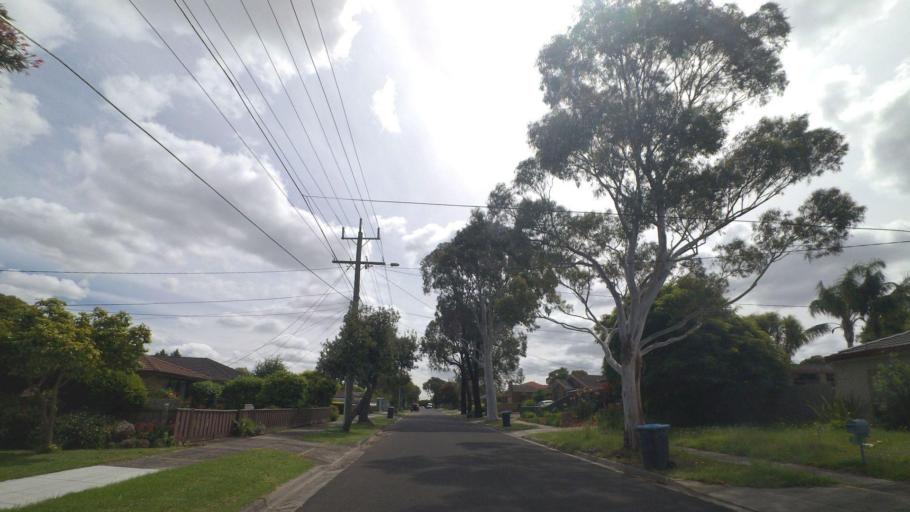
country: AU
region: Victoria
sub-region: Knox
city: Scoresby
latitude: -37.8964
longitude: 145.2358
